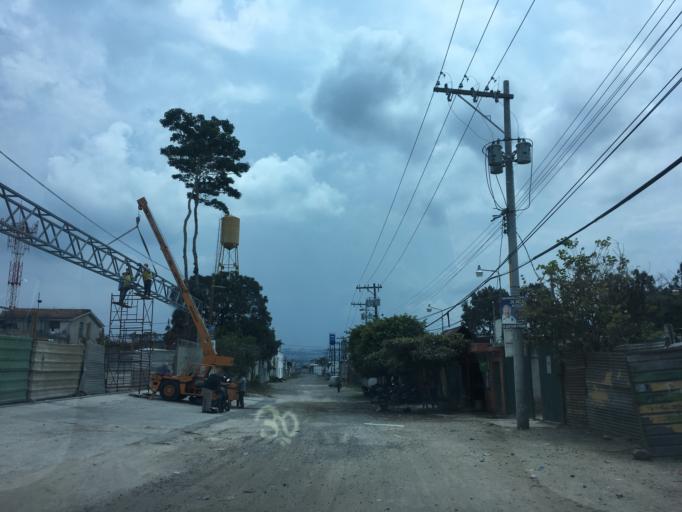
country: GT
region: Guatemala
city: Petapa
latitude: 14.5062
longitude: -90.5578
